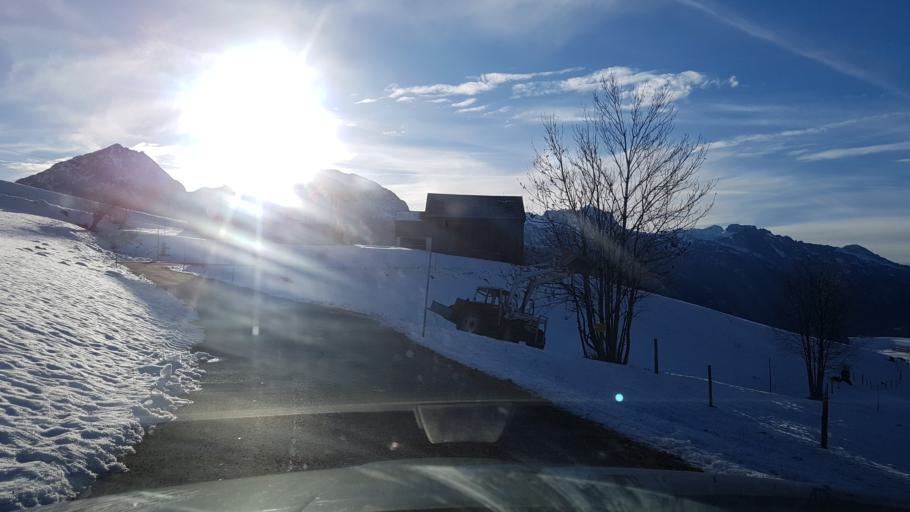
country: AT
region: Salzburg
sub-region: Politischer Bezirk Hallein
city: Abtenau
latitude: 47.5727
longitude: 13.4100
